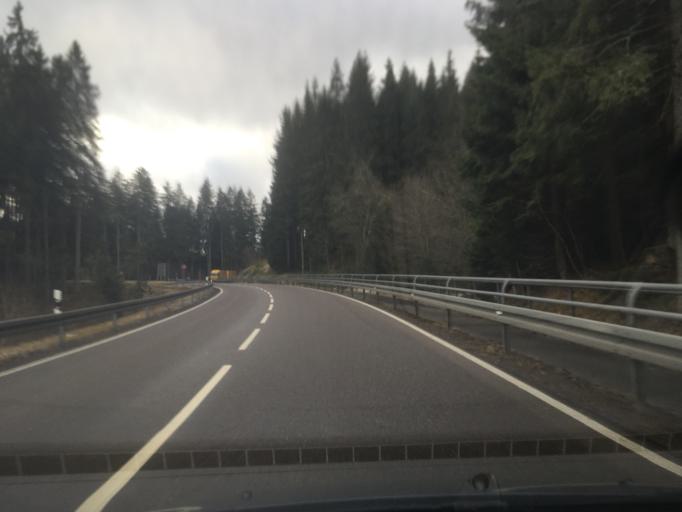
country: DE
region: Baden-Wuerttemberg
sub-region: Freiburg Region
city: Hinterzarten
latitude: 47.8520
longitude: 8.1225
